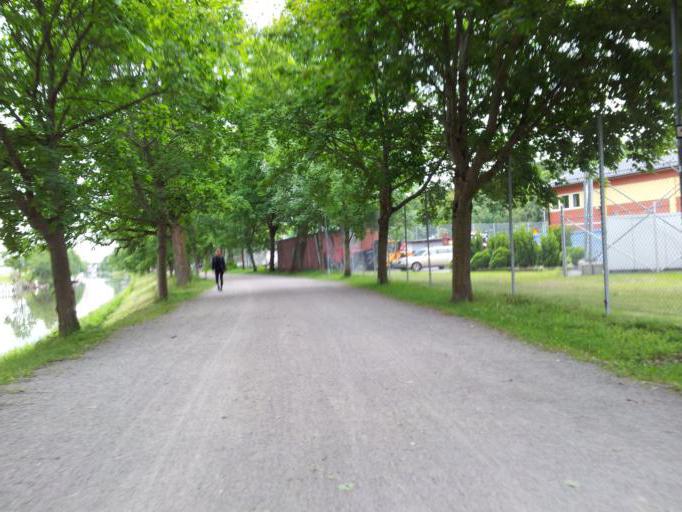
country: SE
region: Uppsala
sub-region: Uppsala Kommun
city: Uppsala
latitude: 59.8481
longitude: 17.6486
